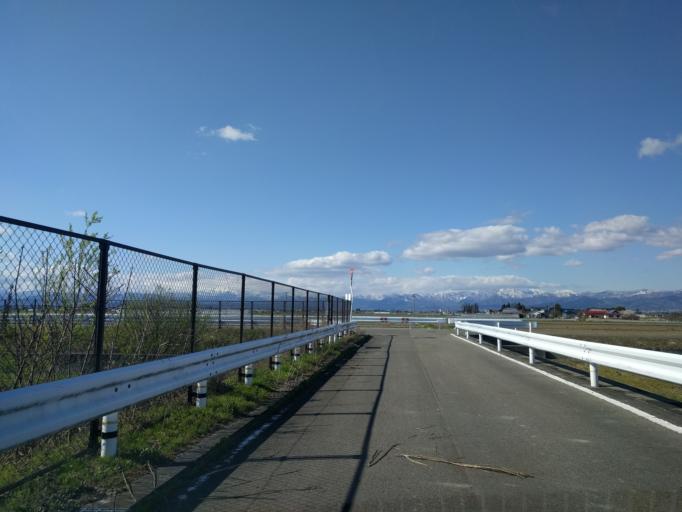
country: JP
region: Fukushima
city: Kitakata
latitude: 37.5452
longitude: 139.8822
